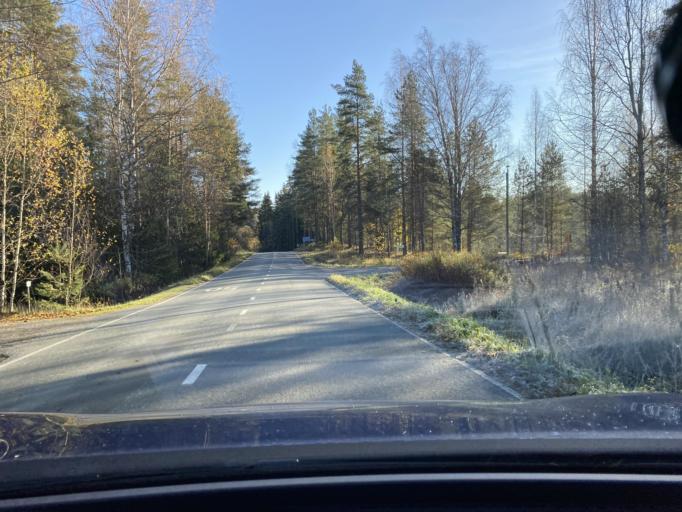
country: FI
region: Pirkanmaa
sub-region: Etelae-Pirkanmaa
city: Kylmaekoski
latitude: 61.0627
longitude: 23.6470
